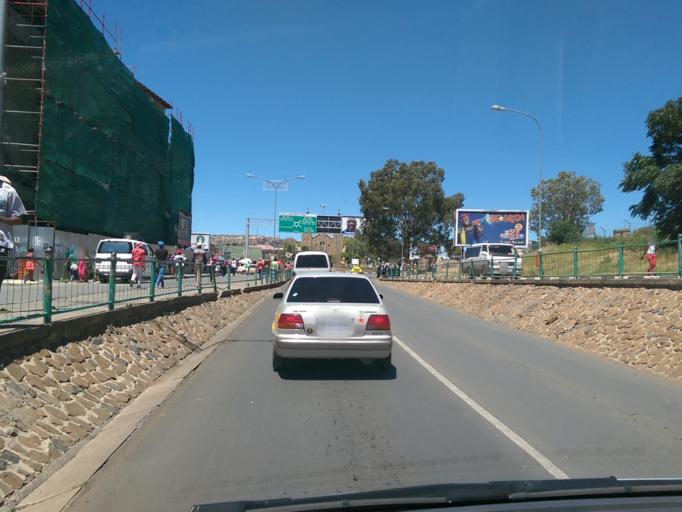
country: LS
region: Maseru
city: Maseru
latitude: -29.3158
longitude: 27.4921
